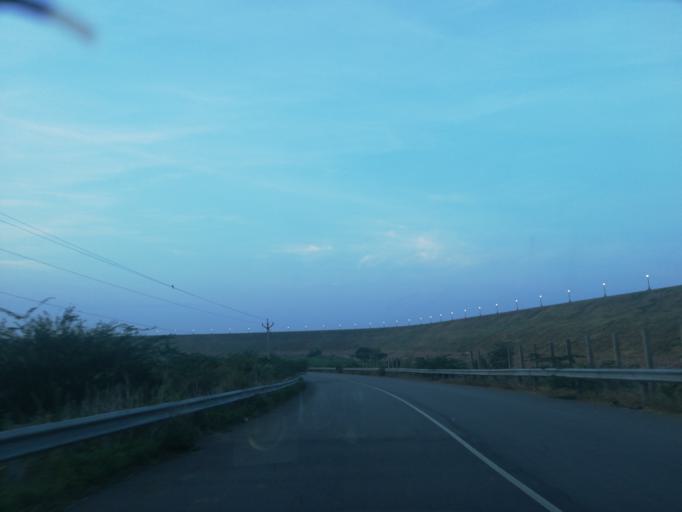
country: IN
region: Andhra Pradesh
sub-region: Guntur
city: Macherla
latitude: 16.5987
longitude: 79.3073
